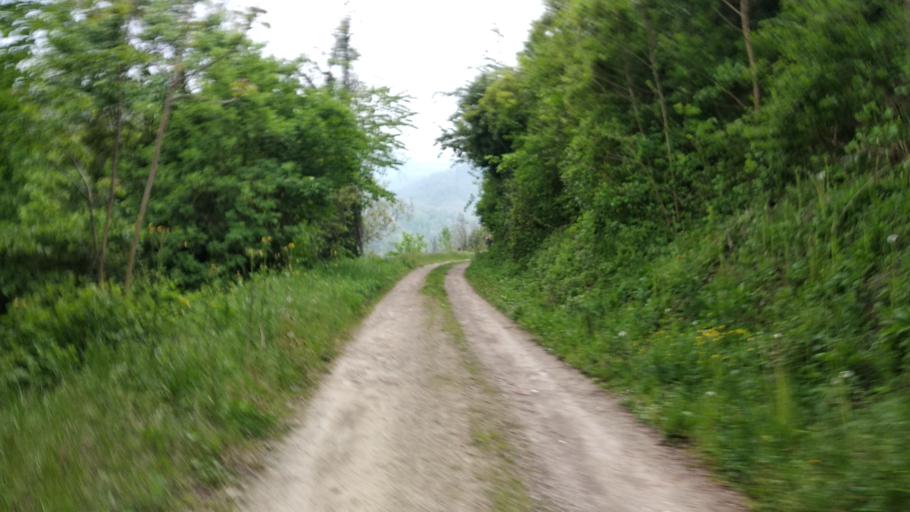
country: IT
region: Emilia-Romagna
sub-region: Forli-Cesena
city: Modigliana
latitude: 44.1502
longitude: 11.7966
